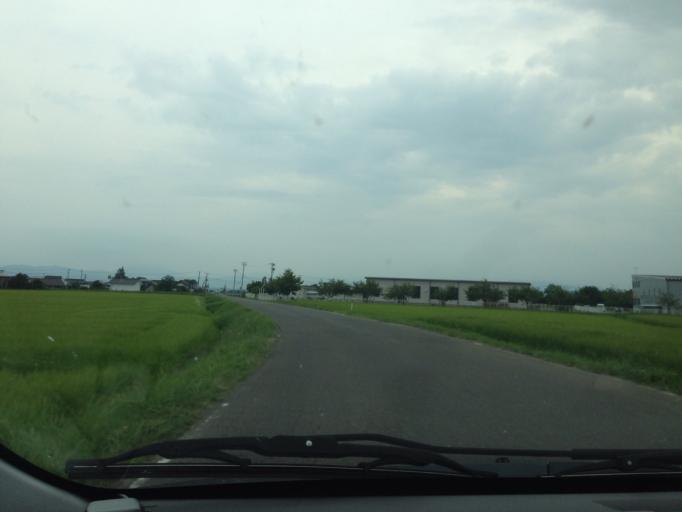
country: JP
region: Fukushima
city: Kitakata
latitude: 37.6495
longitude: 139.8453
